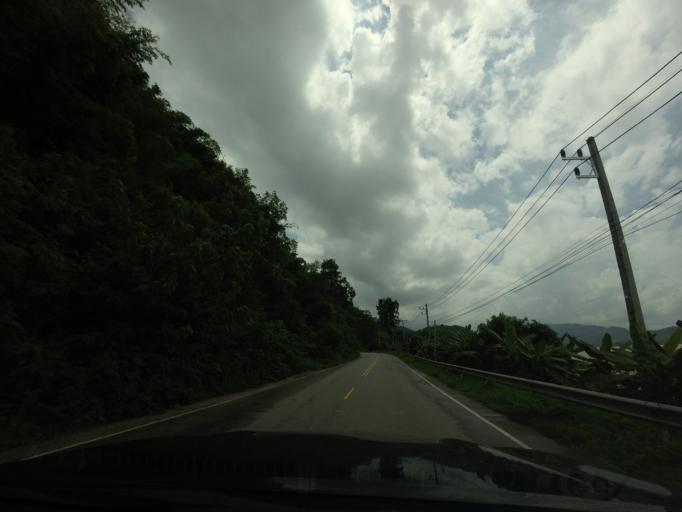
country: TH
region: Loei
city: Pak Chom
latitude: 18.0514
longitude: 101.7755
